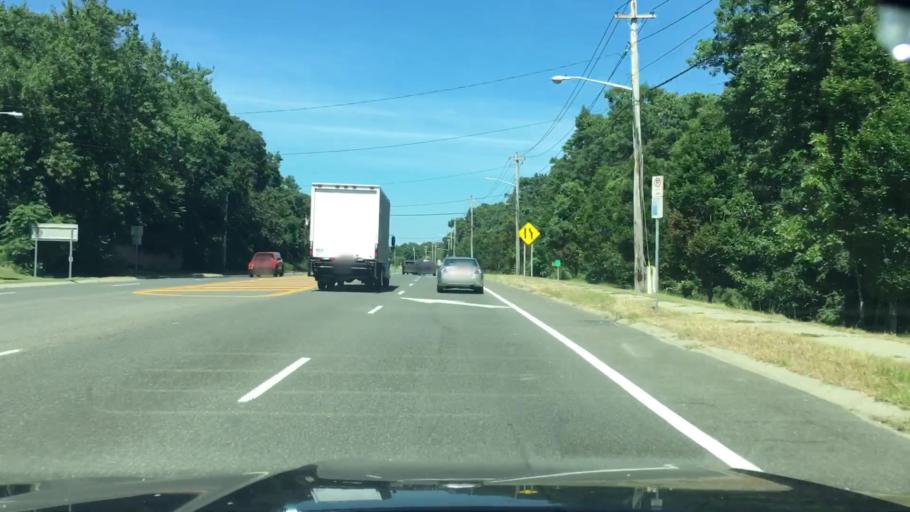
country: US
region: New York
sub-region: Suffolk County
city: Coram
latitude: 40.8856
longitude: -73.0117
